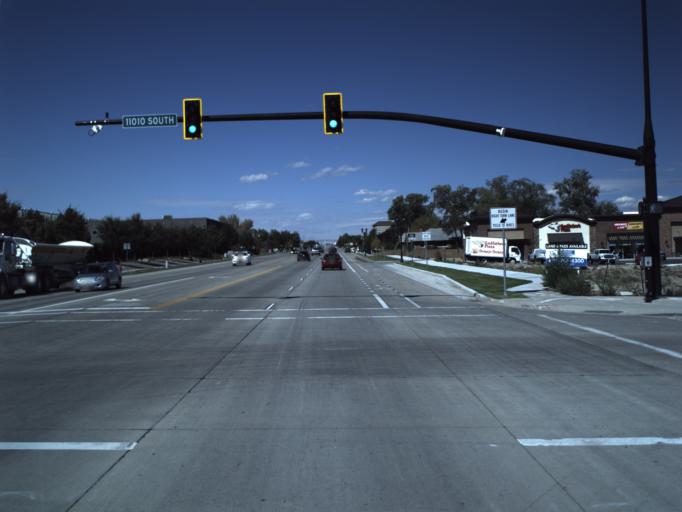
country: US
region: Utah
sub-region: Salt Lake County
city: South Jordan
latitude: 40.5511
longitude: -111.9386
